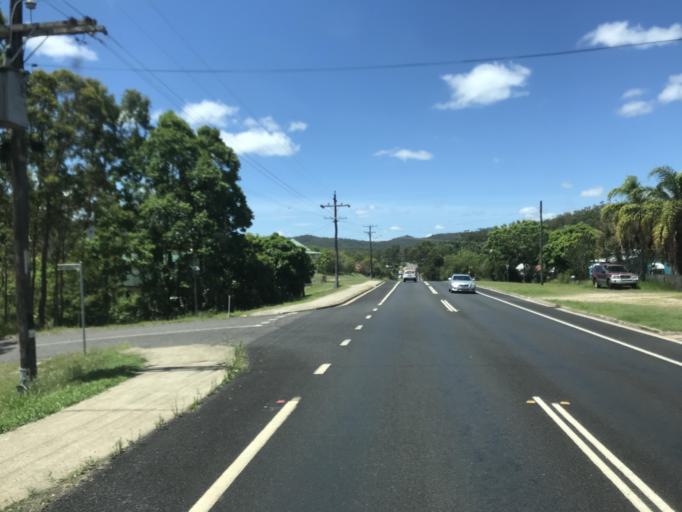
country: AU
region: Queensland
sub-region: Tablelands
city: Atherton
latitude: -17.3920
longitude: 145.3874
